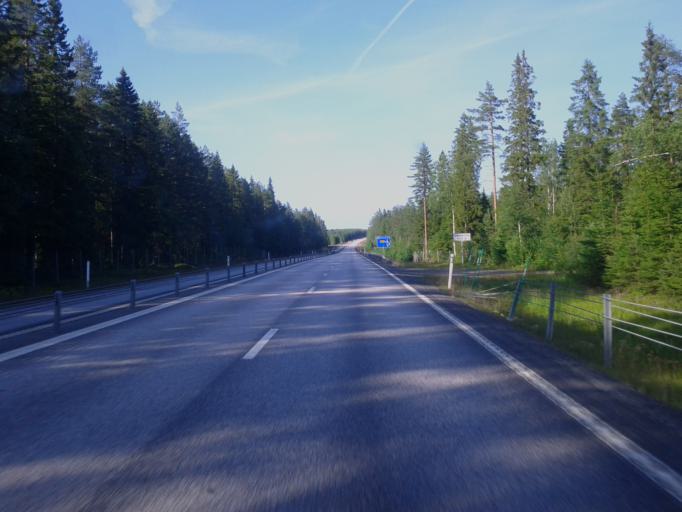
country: SE
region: Vaesterbotten
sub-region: Umea Kommun
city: Saevar
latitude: 63.9777
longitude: 20.7222
